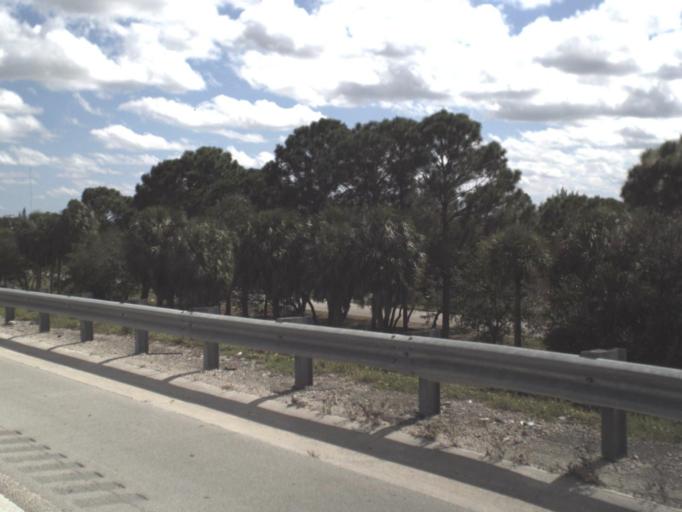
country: US
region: Florida
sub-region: Miami-Dade County
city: Lake Lucerne
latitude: 25.9718
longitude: -80.2618
